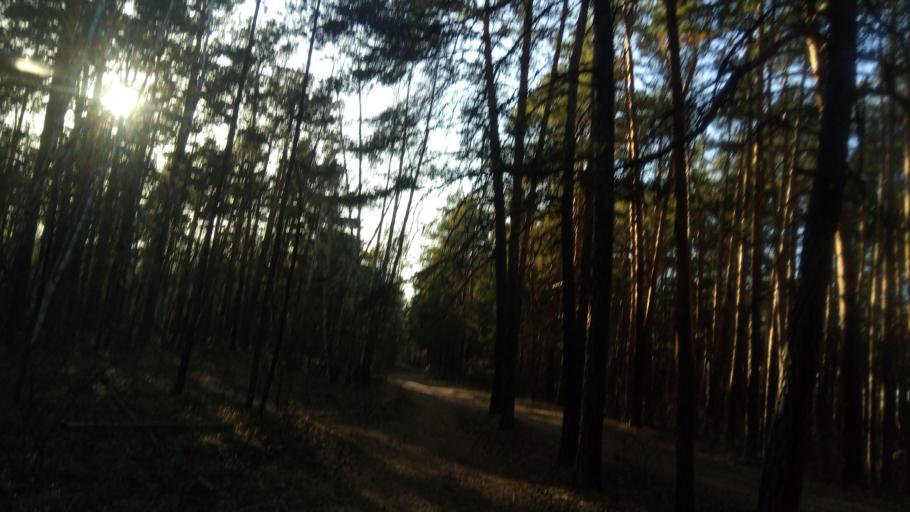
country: RU
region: Chelyabinsk
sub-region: Gorod Chelyabinsk
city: Chelyabinsk
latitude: 55.1598
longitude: 61.3336
